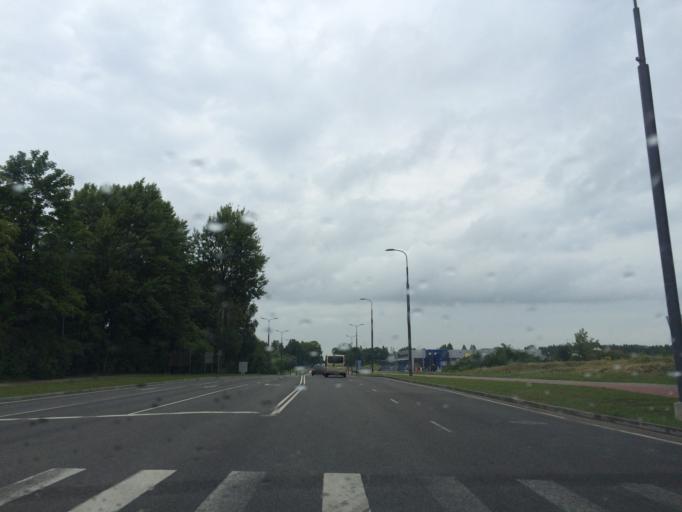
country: LV
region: Rezekne
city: Rezekne
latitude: 56.5294
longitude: 27.3448
